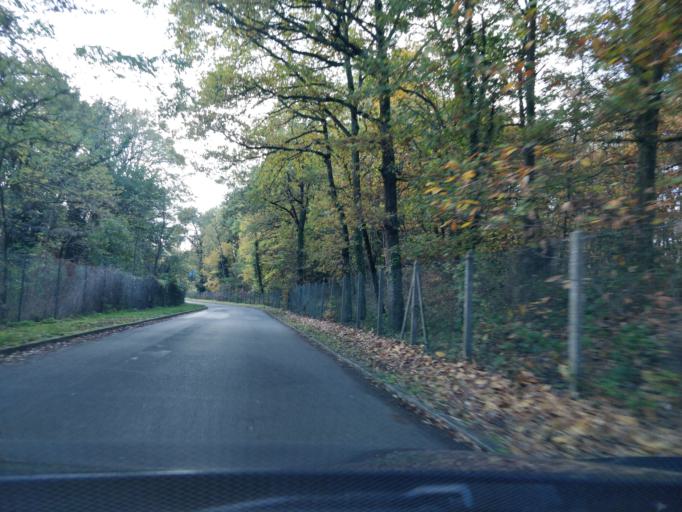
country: FR
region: Ile-de-France
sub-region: Departement de l'Essonne
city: Briis-sous-Forges
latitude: 48.6268
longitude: 2.1317
